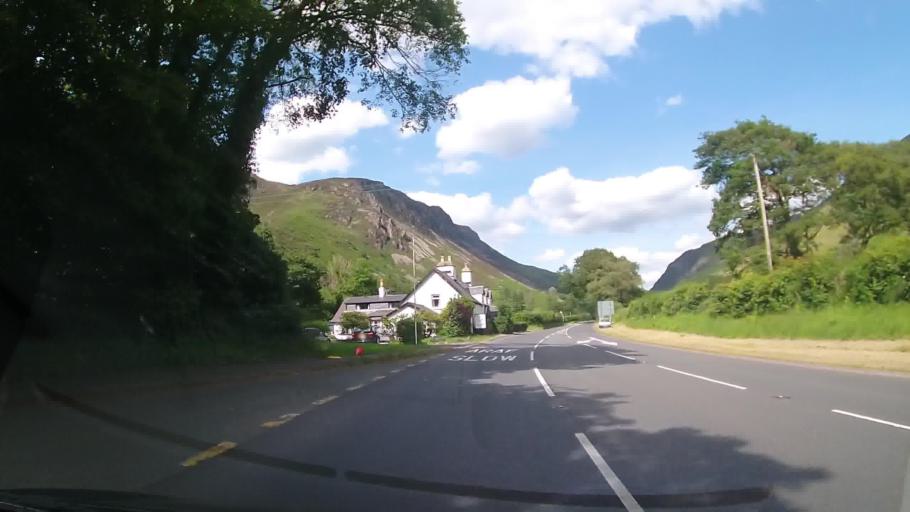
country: GB
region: Wales
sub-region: Gwynedd
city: Corris
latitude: 52.6869
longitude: -3.8758
